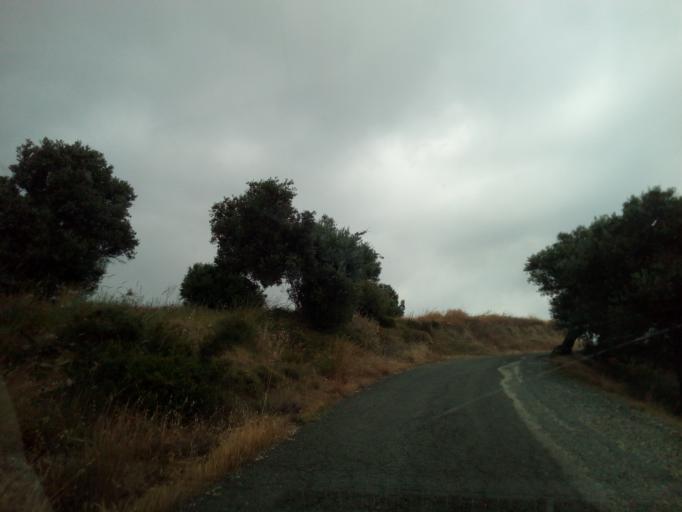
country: CY
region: Pafos
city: Mesogi
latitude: 34.8357
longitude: 32.6177
